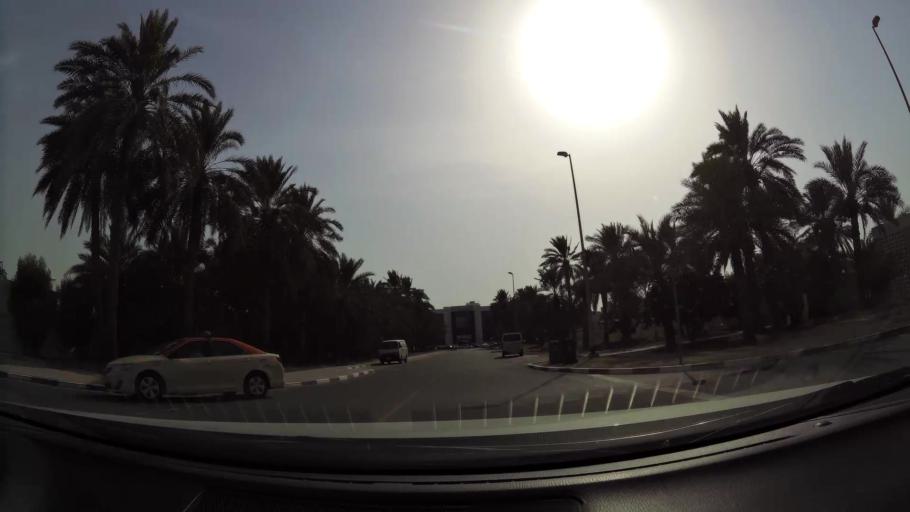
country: AE
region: Ash Shariqah
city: Sharjah
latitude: 25.2517
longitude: 55.4194
